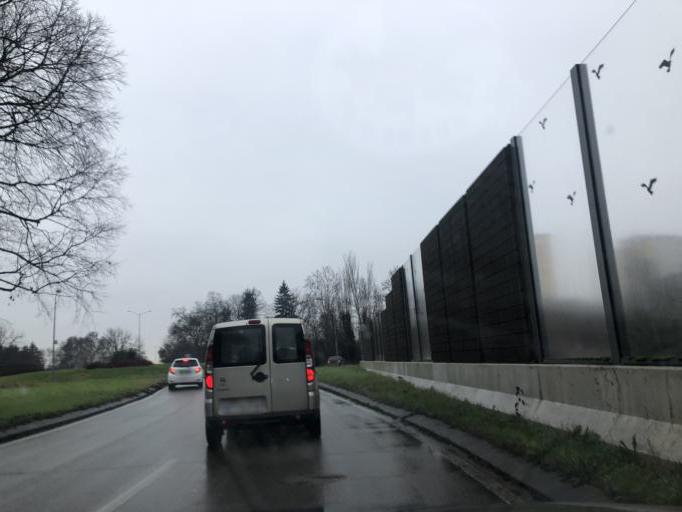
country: IT
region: Emilia-Romagna
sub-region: Provincia di Modena
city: Modena
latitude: 44.6364
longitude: 10.8948
